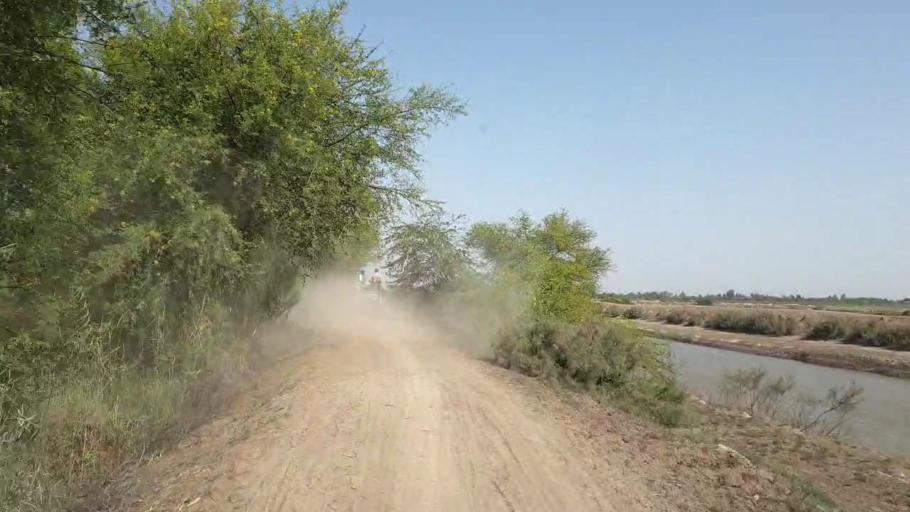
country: PK
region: Sindh
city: Tando Bago
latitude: 24.6691
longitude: 69.0680
